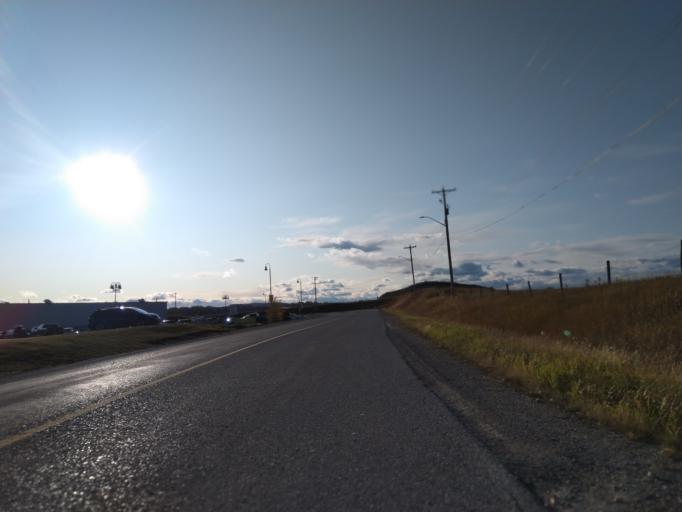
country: CA
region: Alberta
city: Cochrane
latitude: 51.1770
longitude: -114.4525
